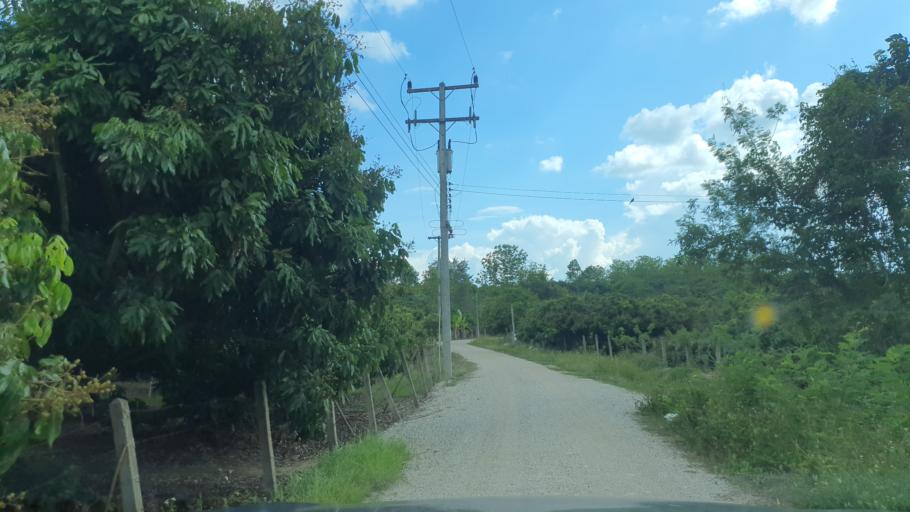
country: TH
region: Chiang Mai
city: Mae Taeng
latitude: 19.1242
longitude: 99.0540
